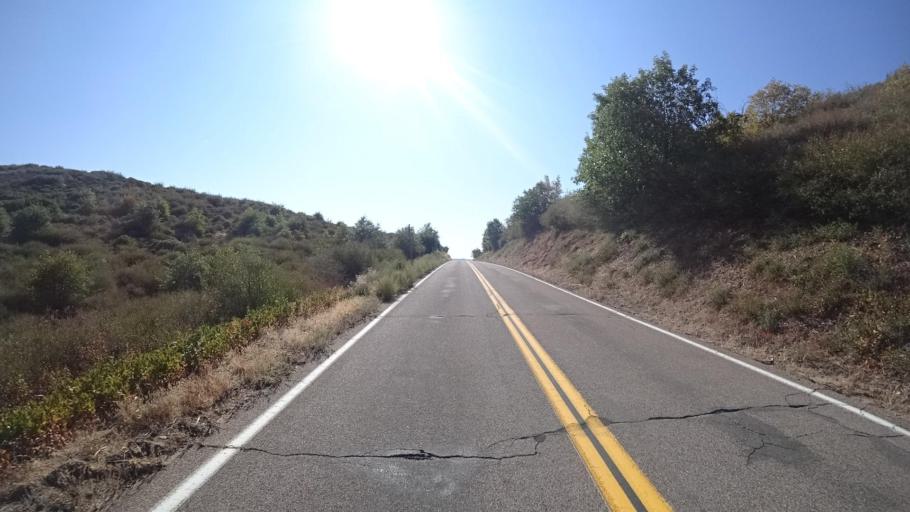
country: US
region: California
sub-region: San Diego County
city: Pine Valley
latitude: 32.9230
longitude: -116.4756
